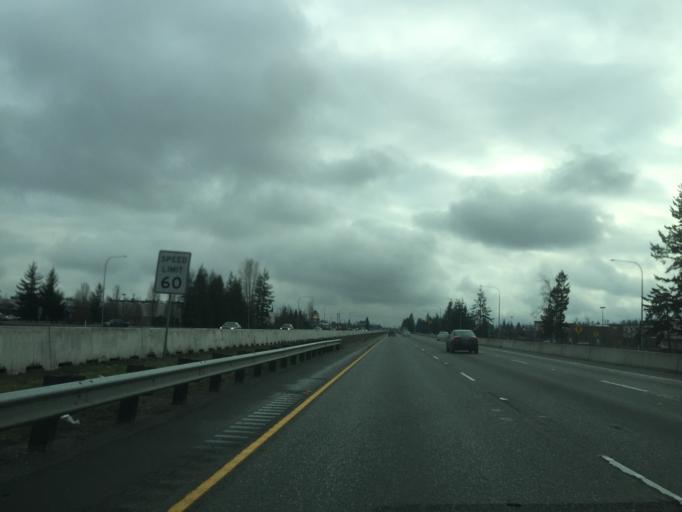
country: US
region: Washington
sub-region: Snohomish County
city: Smokey Point
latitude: 48.1520
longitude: -122.1888
